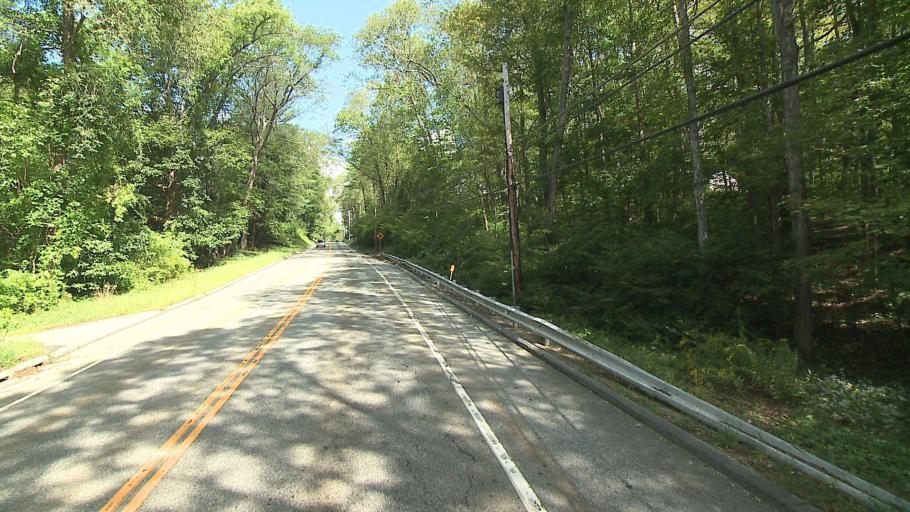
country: US
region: Connecticut
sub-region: Windham County
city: South Woodstock
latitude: 41.8766
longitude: -71.9616
